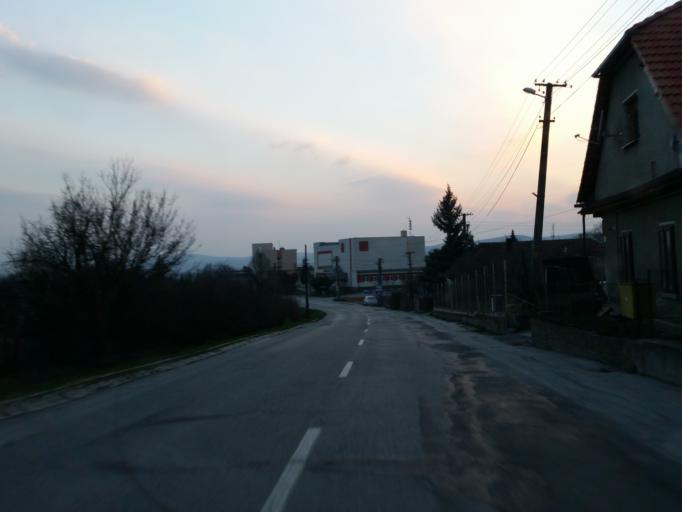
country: SK
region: Trnavsky
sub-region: Okres Trnava
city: Piestany
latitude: 48.5554
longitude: 17.9731
